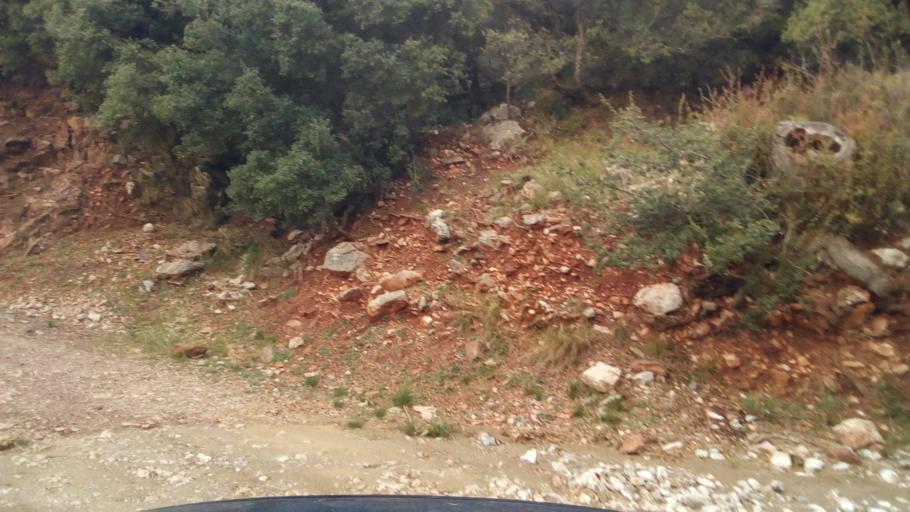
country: GR
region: West Greece
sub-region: Nomos Achaias
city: Kamarai
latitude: 38.4157
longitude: 22.0477
